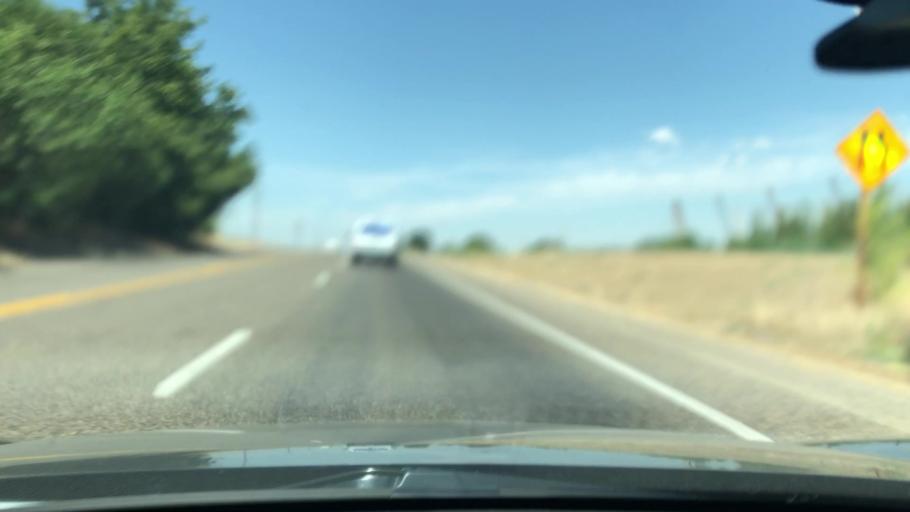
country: US
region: Idaho
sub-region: Canyon County
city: Wilder
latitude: 43.6606
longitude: -116.9117
